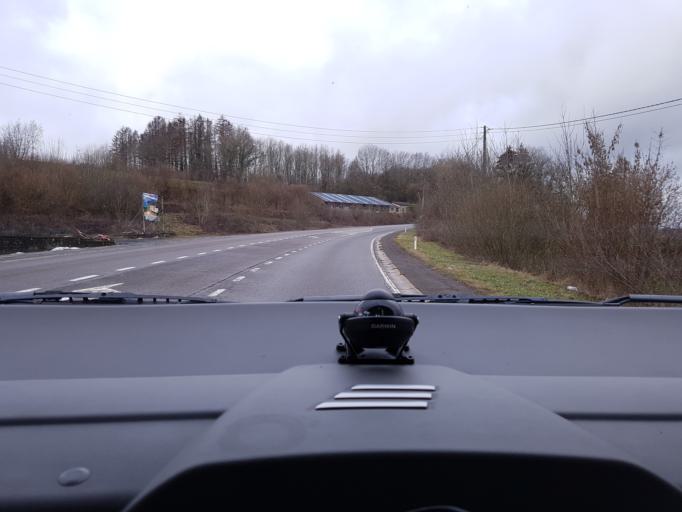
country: LU
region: Luxembourg
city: Eischen
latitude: 49.6578
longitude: 5.8562
